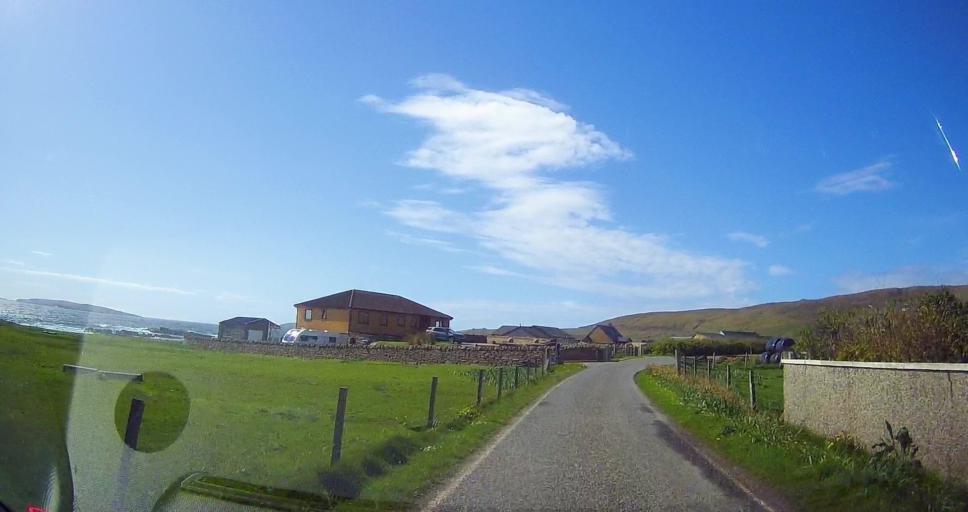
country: GB
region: Scotland
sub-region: Shetland Islands
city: Sandwick
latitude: 60.0361
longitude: -1.2182
